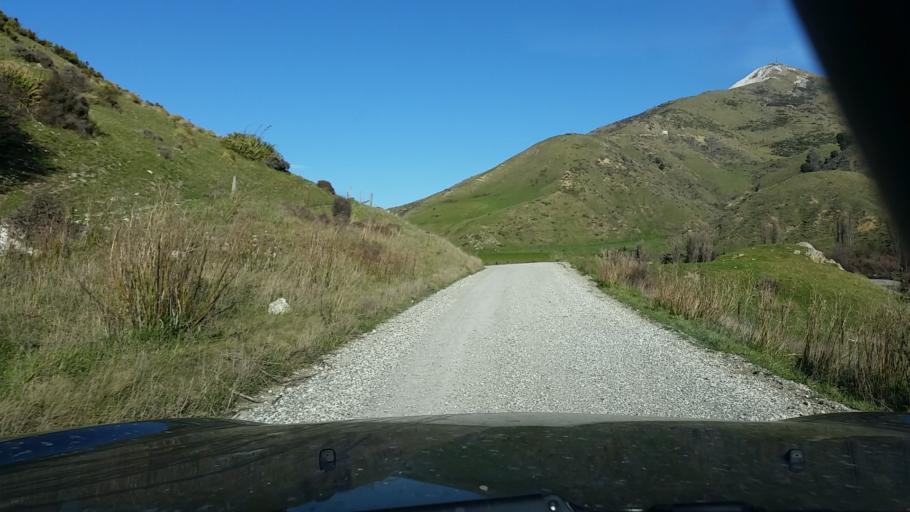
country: NZ
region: Marlborough
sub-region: Marlborough District
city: Blenheim
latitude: -41.8350
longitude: 174.1760
